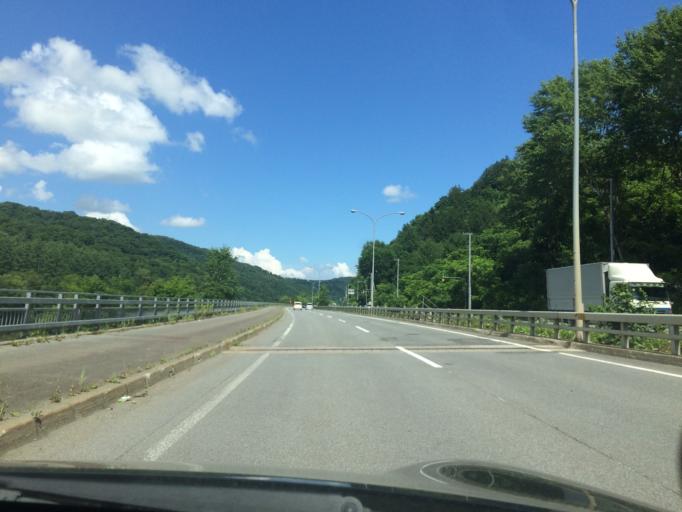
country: JP
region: Hokkaido
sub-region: Asahikawa-shi
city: Asahikawa
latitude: 43.7268
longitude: 142.2187
